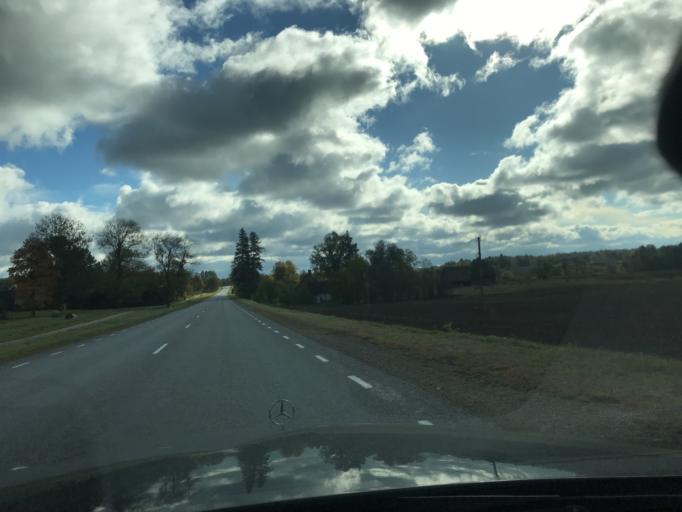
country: EE
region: Vorumaa
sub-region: Antsla vald
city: Vana-Antsla
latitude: 57.9491
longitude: 26.2904
